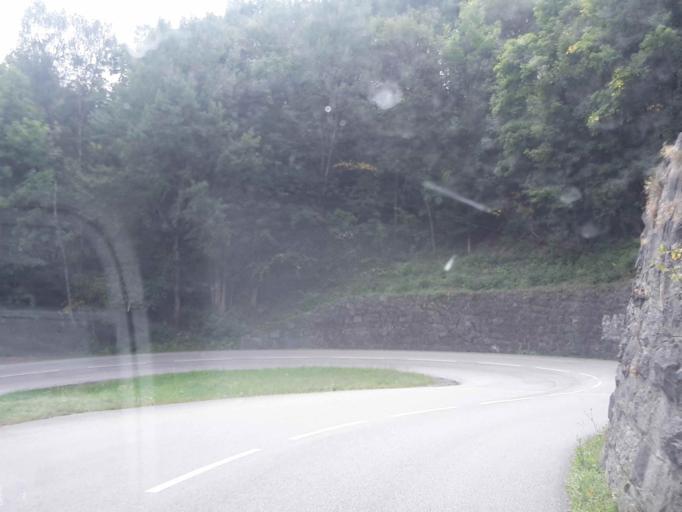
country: FR
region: Rhone-Alpes
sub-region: Departement de la Savoie
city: Saint-Michel-de-Maurienne
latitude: 45.1964
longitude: 6.4683
